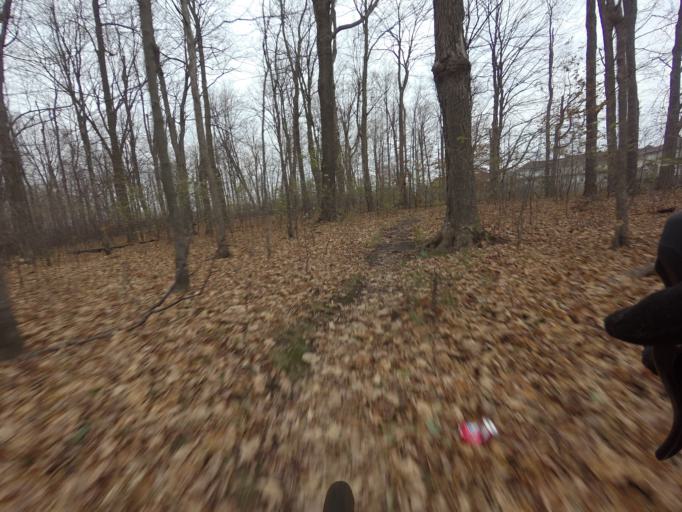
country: CA
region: Ontario
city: Bells Corners
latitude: 45.2720
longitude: -75.7138
